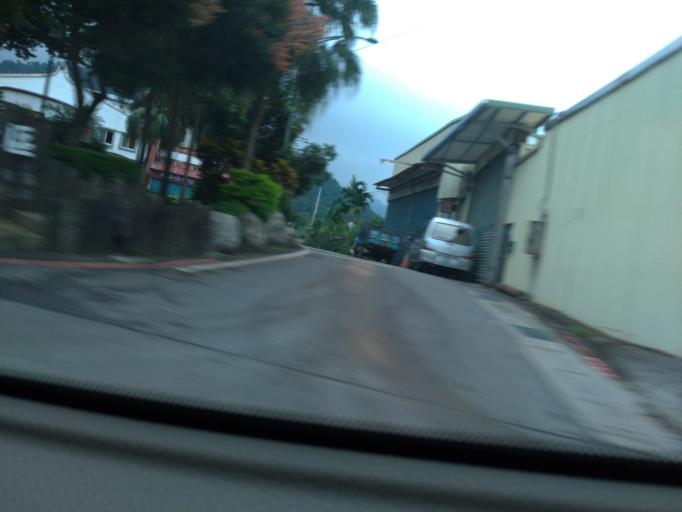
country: TW
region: Taipei
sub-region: Taipei
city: Banqiao
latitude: 24.9321
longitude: 121.4076
